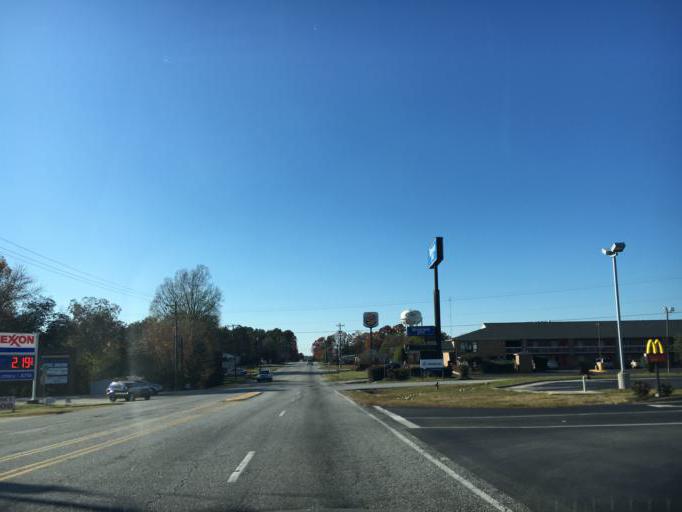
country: US
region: South Carolina
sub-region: Spartanburg County
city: Southern Shops
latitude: 34.9913
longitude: -82.0219
